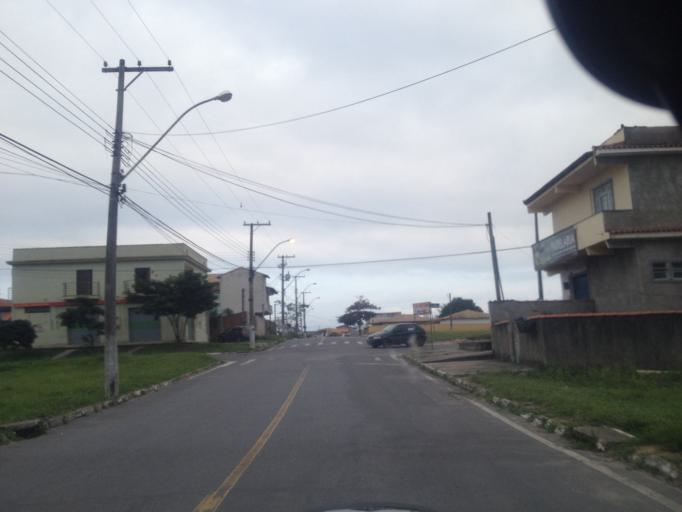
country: BR
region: Rio de Janeiro
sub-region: Porto Real
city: Porto Real
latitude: -22.4119
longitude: -44.3087
